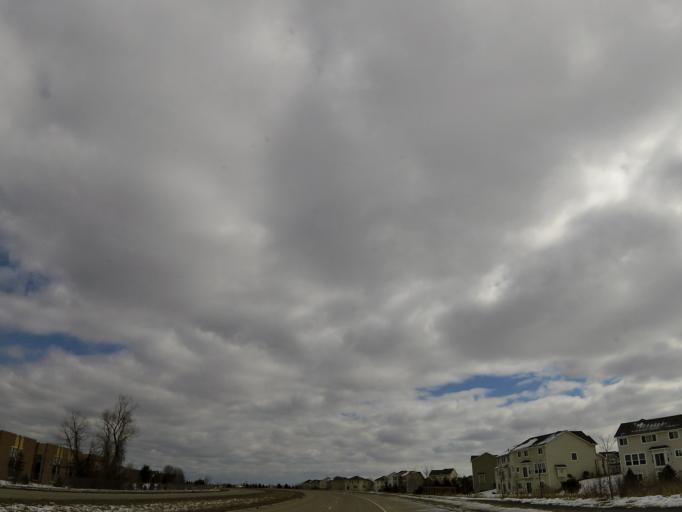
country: US
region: Minnesota
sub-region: Scott County
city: Prior Lake
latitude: 44.7722
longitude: -93.4220
